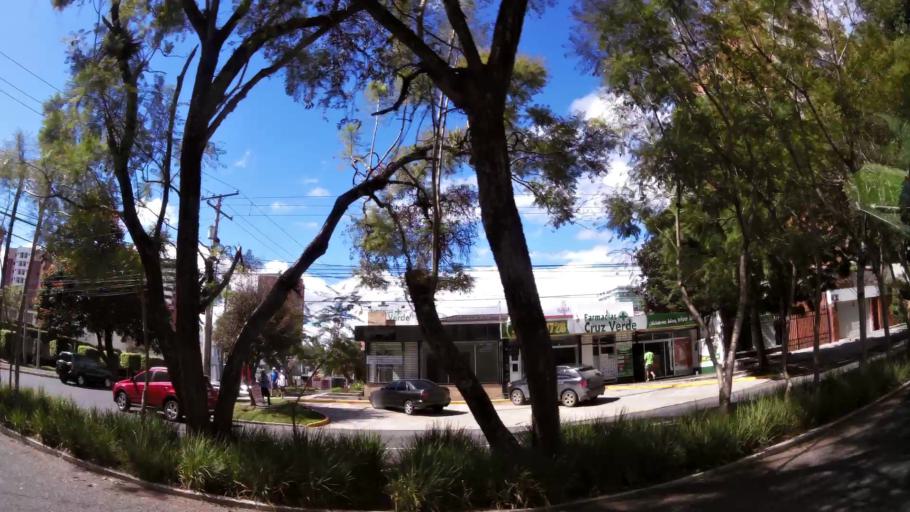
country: GT
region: Guatemala
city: Santa Catarina Pinula
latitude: 14.5795
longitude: -90.5190
